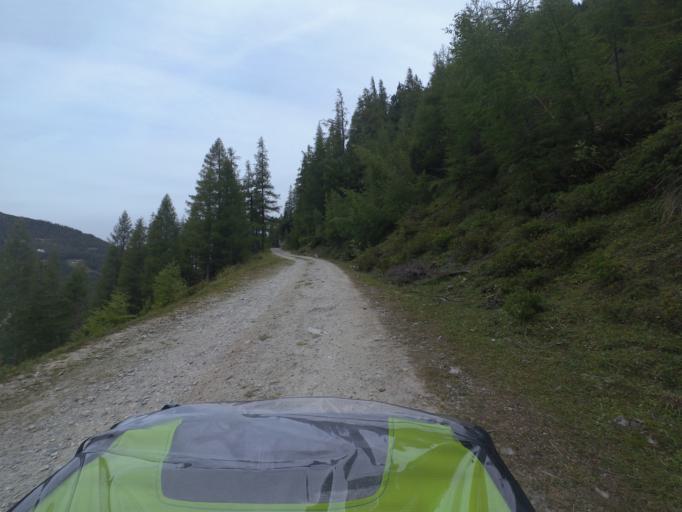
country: AT
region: Salzburg
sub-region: Politischer Bezirk Sankt Johann im Pongau
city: Untertauern
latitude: 47.2923
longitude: 13.5825
